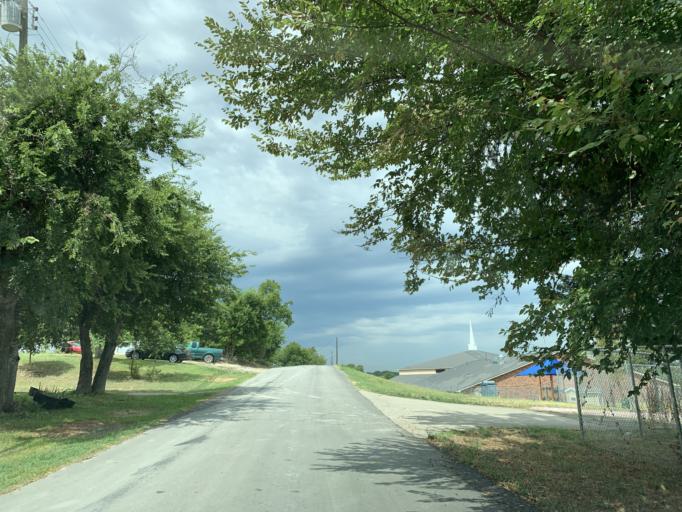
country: US
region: Texas
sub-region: Dallas County
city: Duncanville
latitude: 32.6725
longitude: -96.8329
